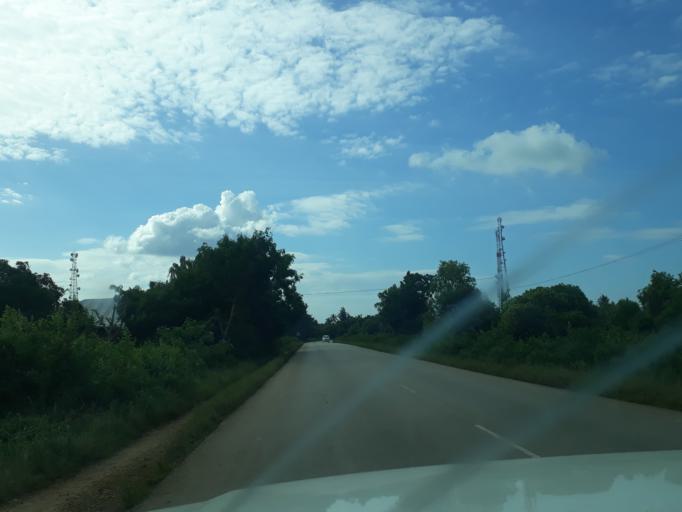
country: TZ
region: Zanzibar North
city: Nungwi
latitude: -5.7666
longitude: 39.3013
